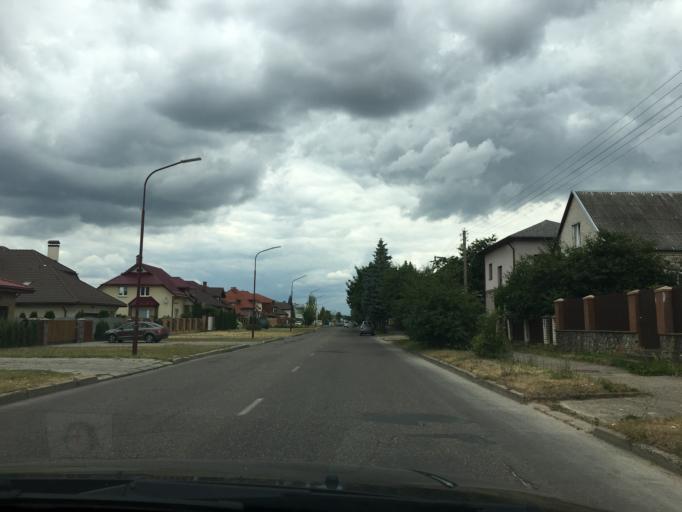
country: BY
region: Grodnenskaya
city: Hrodna
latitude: 53.6264
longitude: 23.8481
